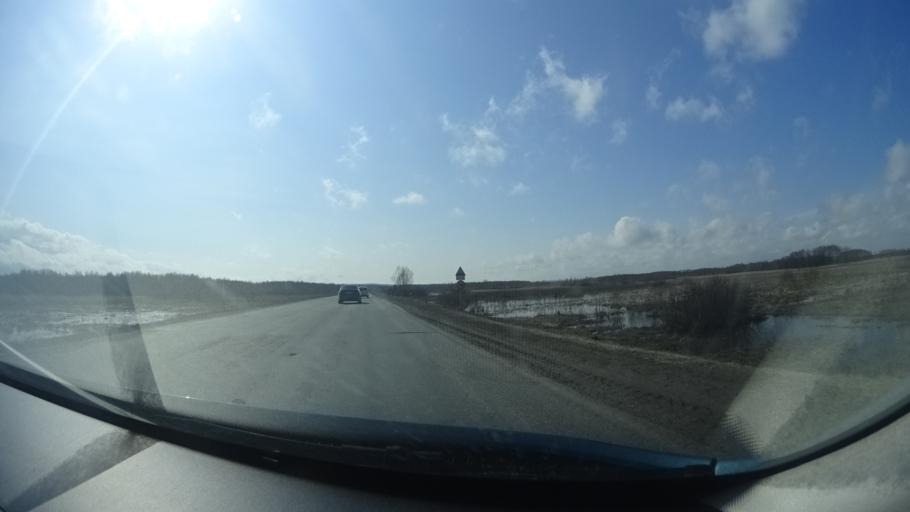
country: RU
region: Bashkortostan
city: Mikhaylovka
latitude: 54.9208
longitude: 55.7365
